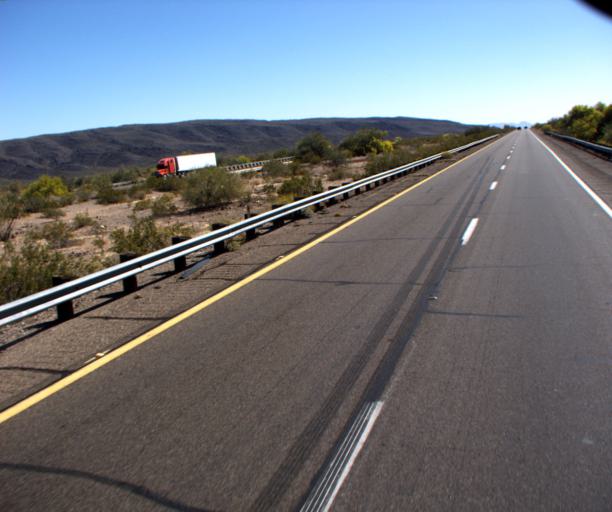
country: US
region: Arizona
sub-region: La Paz County
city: Quartzsite
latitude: 33.6533
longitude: -113.9432
